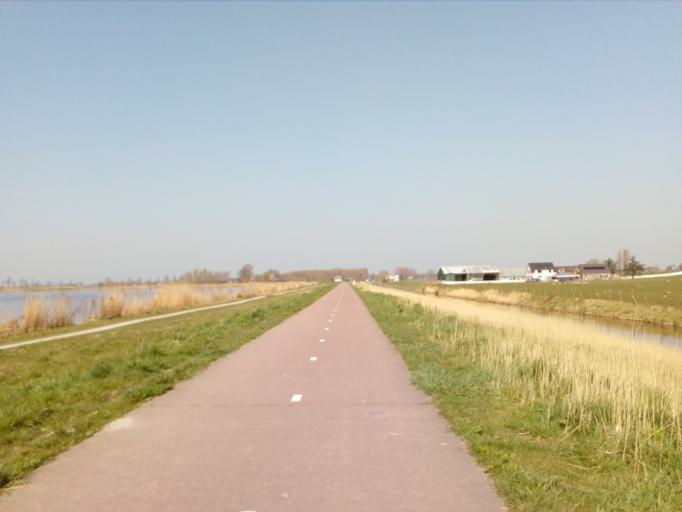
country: NL
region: South Holland
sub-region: Gemeente Rijnwoude
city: Benthuizen
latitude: 52.0805
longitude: 4.5263
